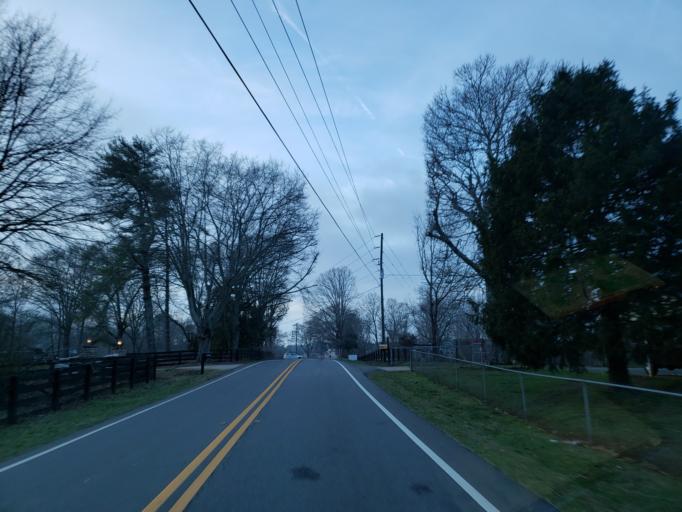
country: US
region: Georgia
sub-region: Fulton County
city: Milton
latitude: 34.2307
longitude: -84.3315
